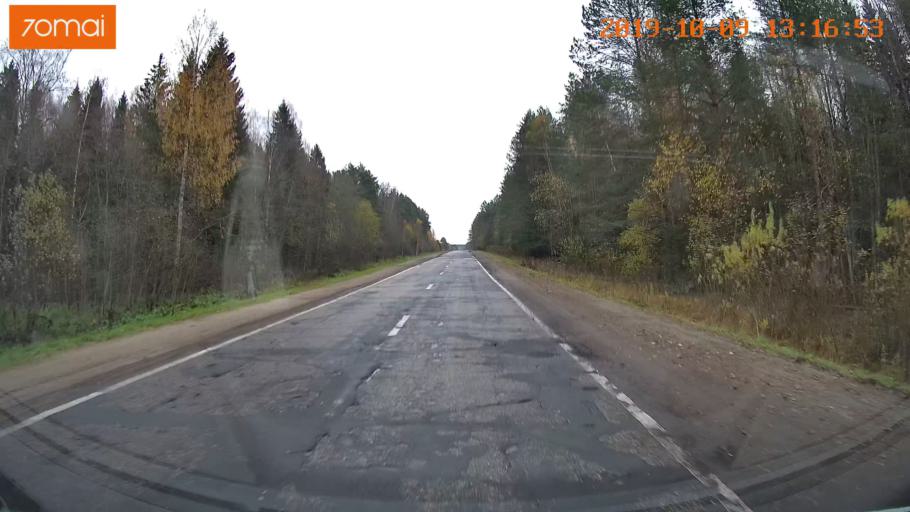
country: RU
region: Jaroslavl
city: Lyubim
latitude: 58.3580
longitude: 40.7720
